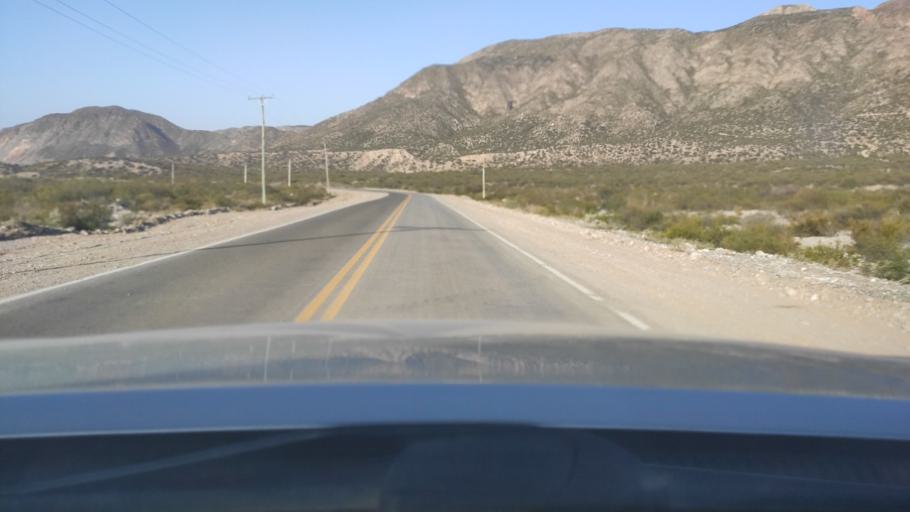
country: AR
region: San Juan
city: Villa Media Agua
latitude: -32.0085
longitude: -68.7730
